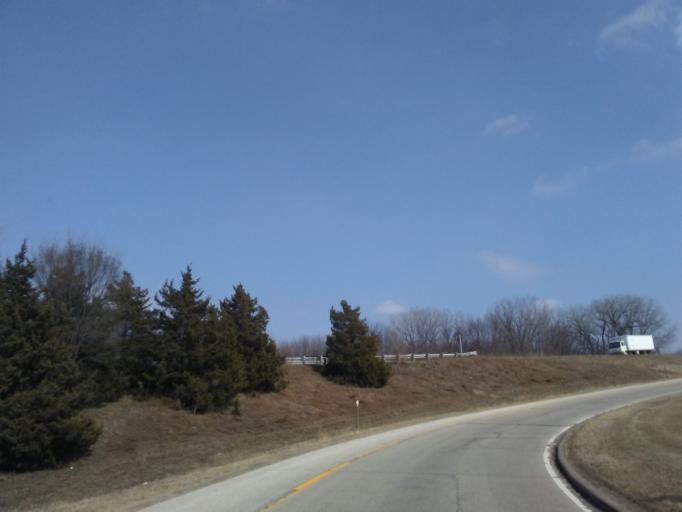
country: US
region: Wisconsin
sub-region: La Crosse County
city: Onalaska
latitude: 43.8668
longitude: -91.2343
